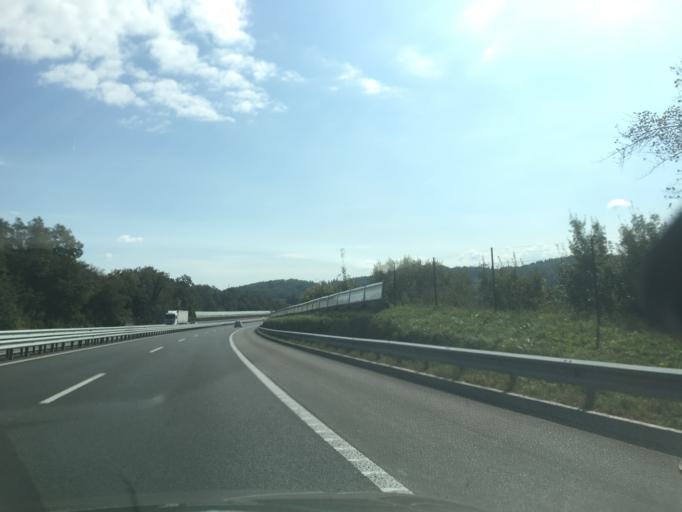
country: SI
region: Ivancna Gorica
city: Ivancna Gorica
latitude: 45.9444
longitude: 14.7785
